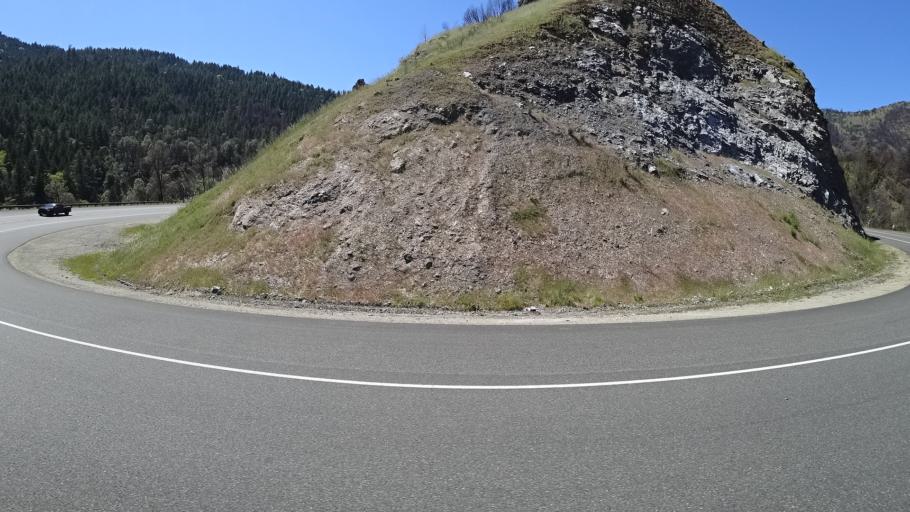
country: US
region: California
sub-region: Trinity County
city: Weaverville
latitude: 40.7610
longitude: -123.0963
